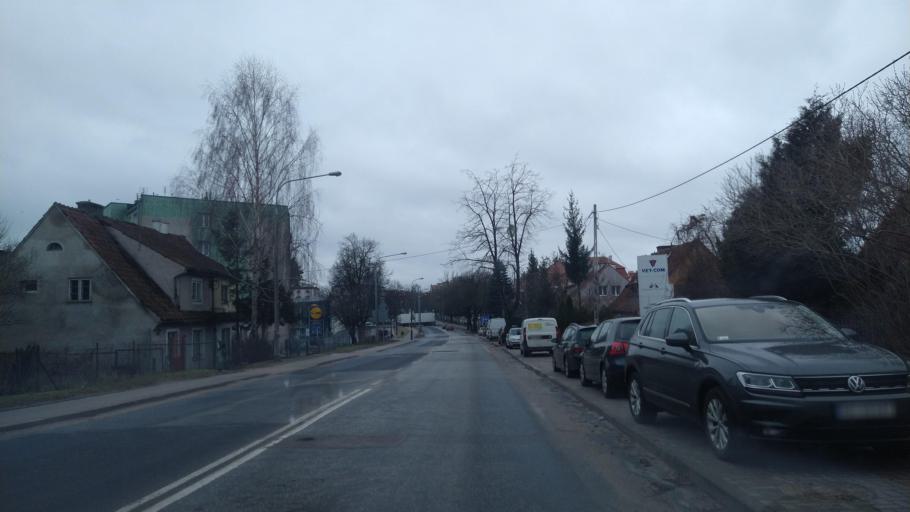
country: PL
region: Warmian-Masurian Voivodeship
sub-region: Powiat olsztynski
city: Olsztyn
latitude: 53.7960
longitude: 20.4986
